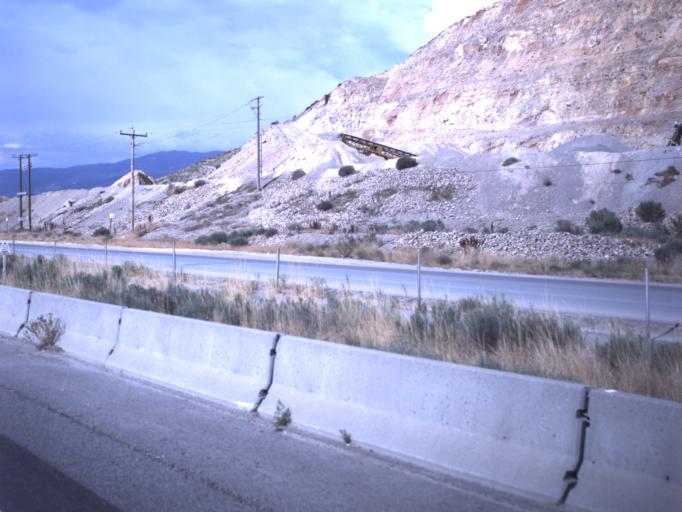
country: US
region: Utah
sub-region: Davis County
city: North Salt Lake
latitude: 40.8278
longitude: -111.9156
